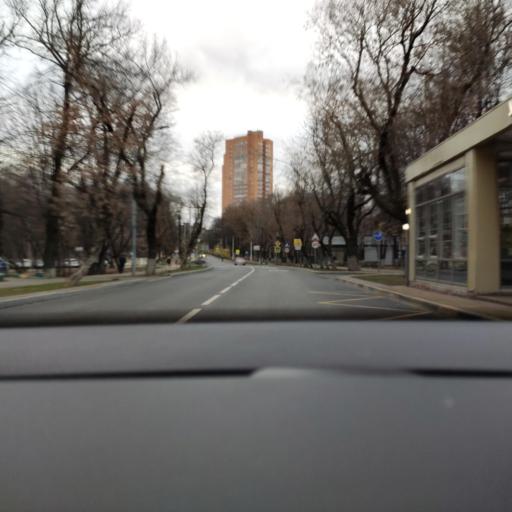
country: RU
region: Moscow
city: Khimki
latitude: 55.8989
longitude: 37.4565
